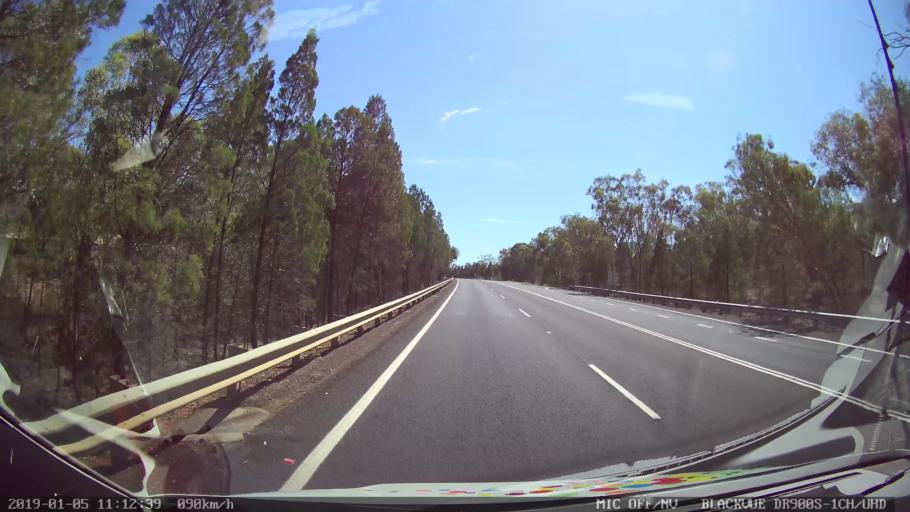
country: AU
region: New South Wales
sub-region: Warrumbungle Shire
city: Coonabarabran
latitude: -31.3799
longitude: 149.2630
